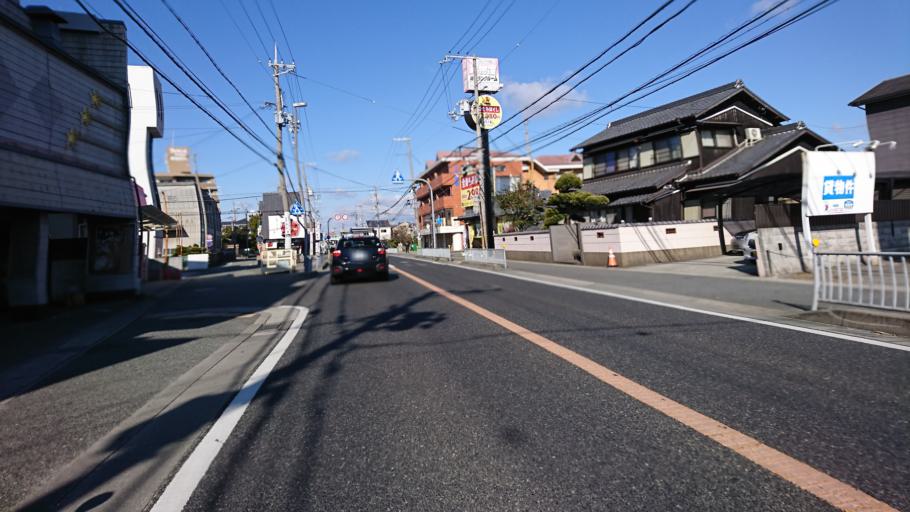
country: JP
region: Hyogo
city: Kakogawacho-honmachi
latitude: 34.7362
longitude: 134.8748
